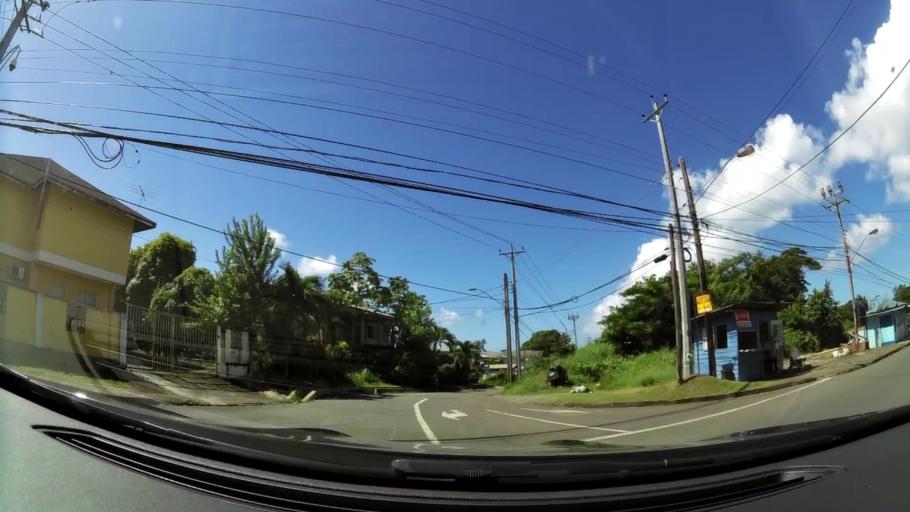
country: TT
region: Tobago
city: Scarborough
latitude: 11.1721
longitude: -60.7995
